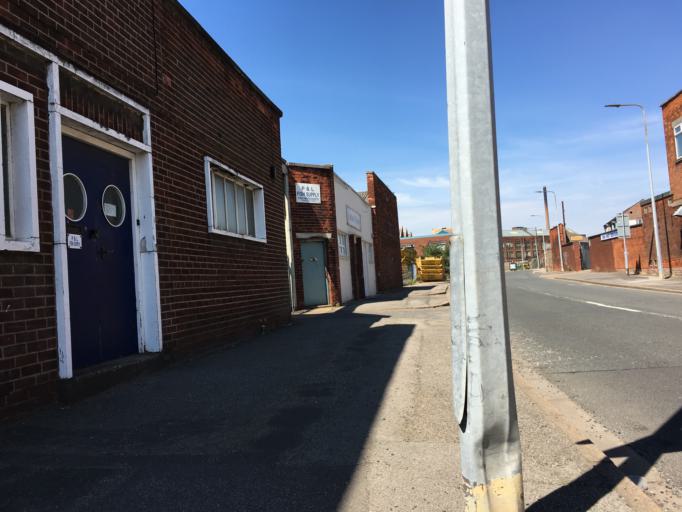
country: GB
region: England
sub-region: City of Kingston upon Hull
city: Hull
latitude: 53.7542
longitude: -0.3304
